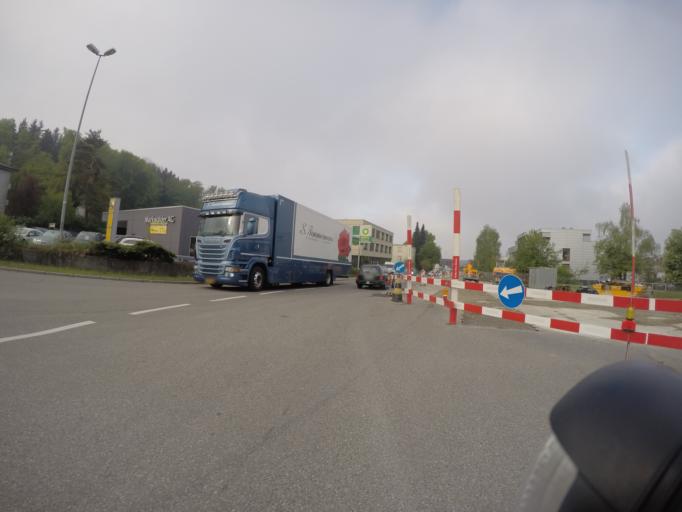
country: CH
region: Zurich
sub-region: Bezirk Pfaeffikon
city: Tagelswangen
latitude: 47.4324
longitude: 8.6764
